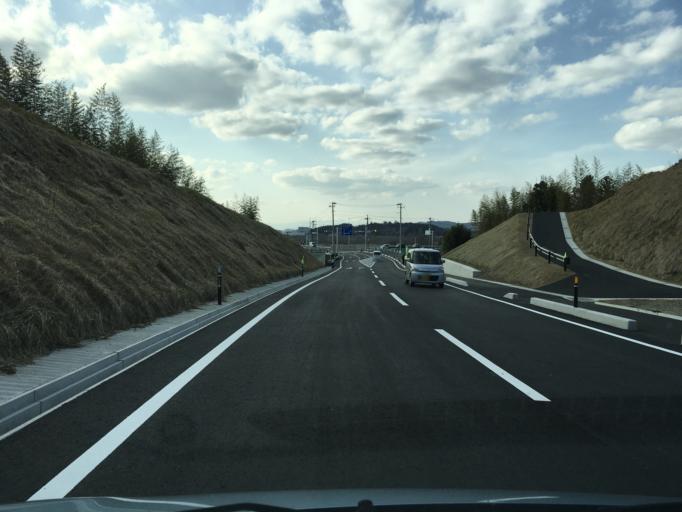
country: JP
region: Miyagi
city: Wakuya
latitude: 38.7228
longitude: 141.2730
